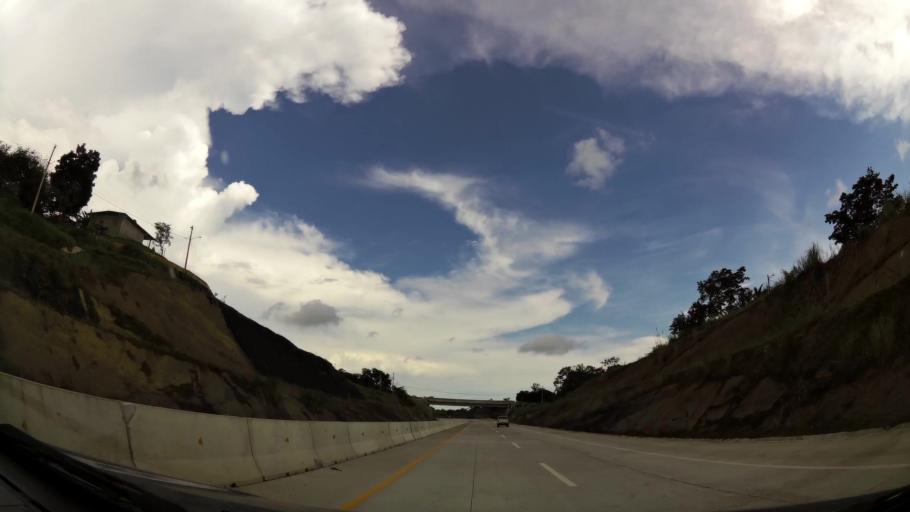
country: PA
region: Panama
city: Tocumen
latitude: 9.1071
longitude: -79.4010
